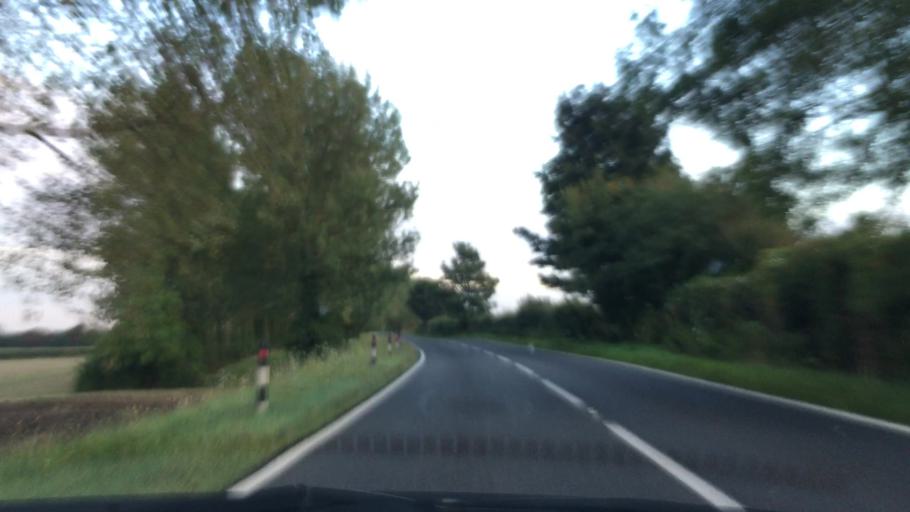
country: GB
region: England
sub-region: North East Lincolnshire
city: Wold Newton
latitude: 53.4702
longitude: -0.1083
